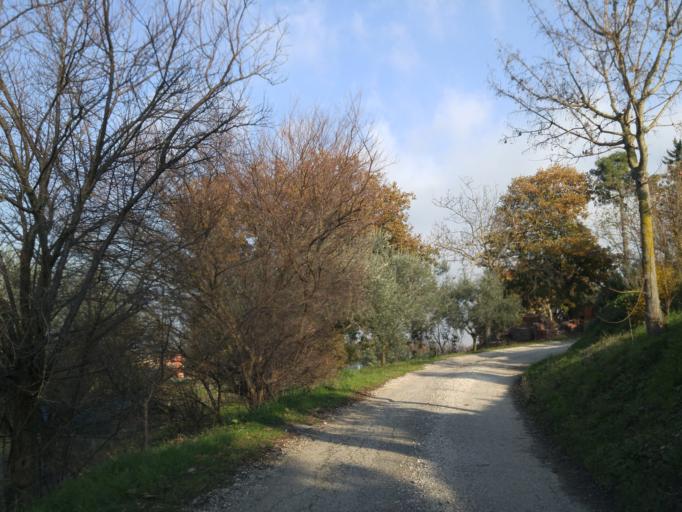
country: IT
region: The Marches
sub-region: Provincia di Pesaro e Urbino
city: Villanova
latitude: 43.7415
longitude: 12.9275
